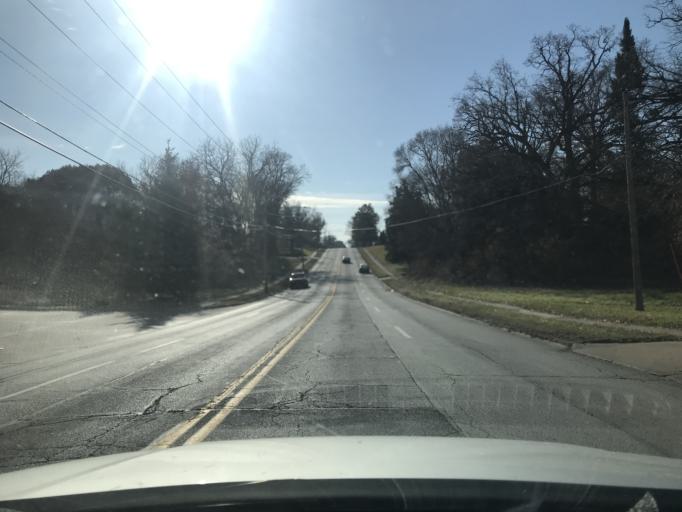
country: US
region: Iowa
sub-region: Scott County
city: Davenport
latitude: 41.5364
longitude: -90.6132
